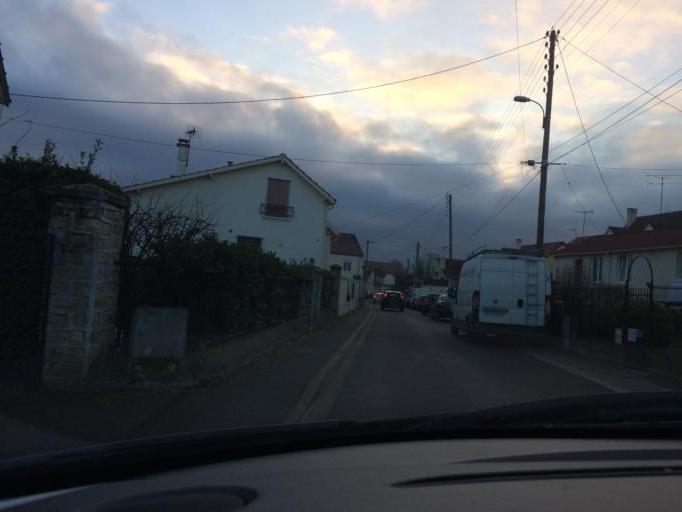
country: FR
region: Ile-de-France
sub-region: Departement de l'Essonne
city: Etrechy
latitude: 48.4960
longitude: 2.1915
